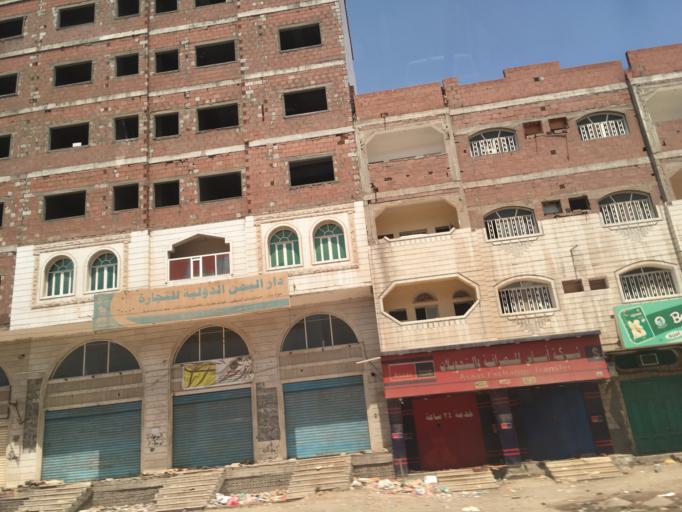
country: YE
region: Aden
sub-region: Al Mansura
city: Al Mansurah
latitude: 12.8664
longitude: 44.9710
